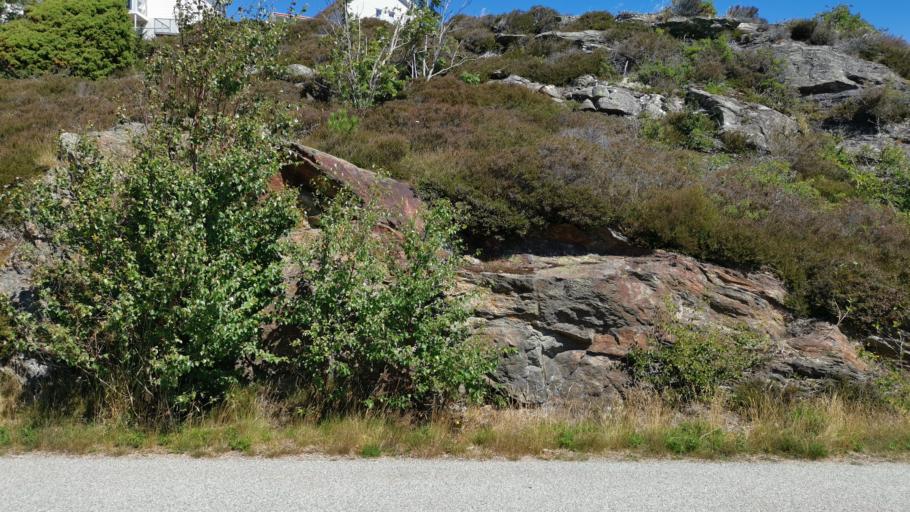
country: SE
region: Vaestra Goetaland
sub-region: Lysekils Kommun
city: Lysekil
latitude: 58.2115
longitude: 11.4258
